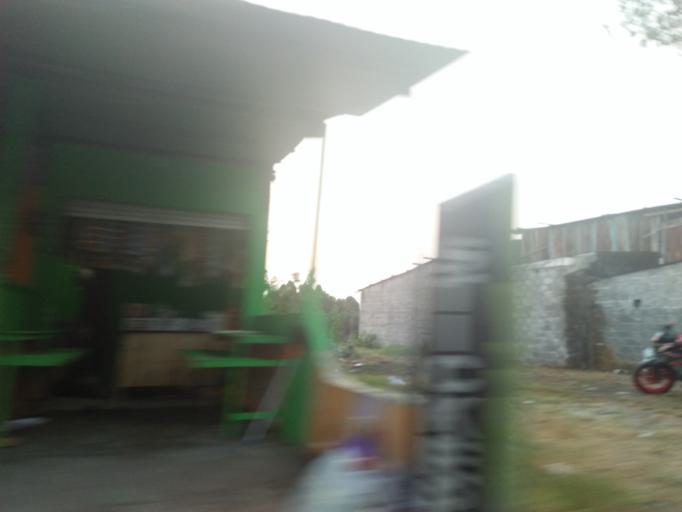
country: ID
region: Daerah Istimewa Yogyakarta
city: Sewon
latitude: -7.8416
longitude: 110.3914
